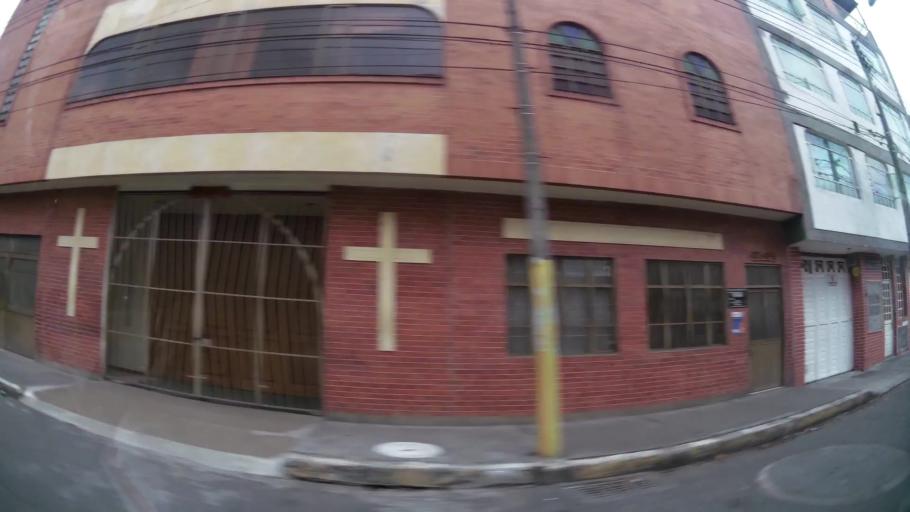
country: CO
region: Bogota D.C.
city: Barrio San Luis
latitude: 4.7001
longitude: -74.1051
